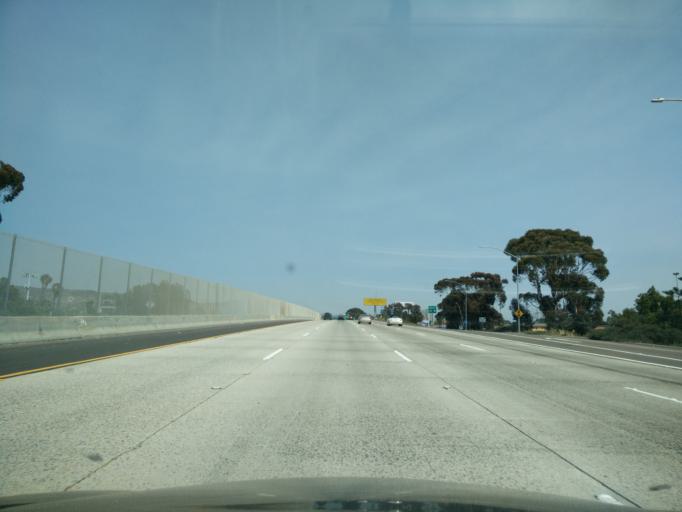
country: MX
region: Baja California
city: Tijuana
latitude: 32.5525
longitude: -117.0482
